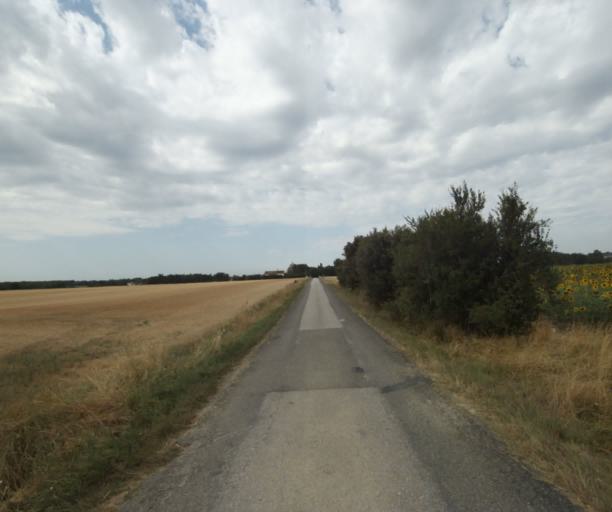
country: FR
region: Midi-Pyrenees
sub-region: Departement de la Haute-Garonne
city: Saint-Felix-Lauragais
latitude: 43.4437
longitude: 1.9297
